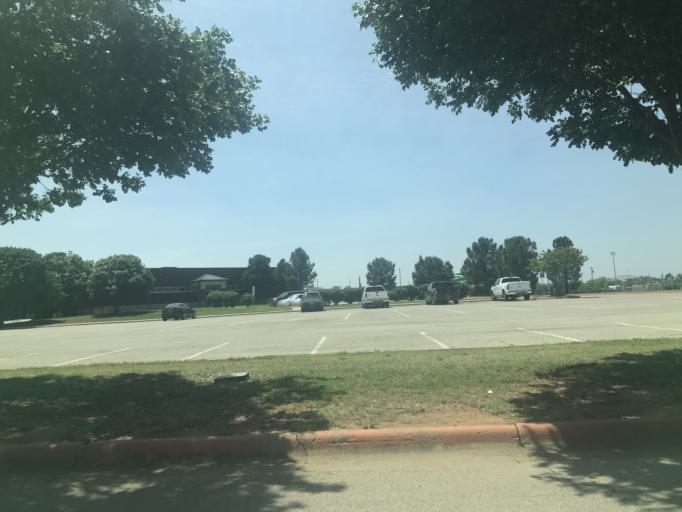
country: US
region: Texas
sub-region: Taylor County
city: Abilene
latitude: 32.4421
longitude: -99.7556
